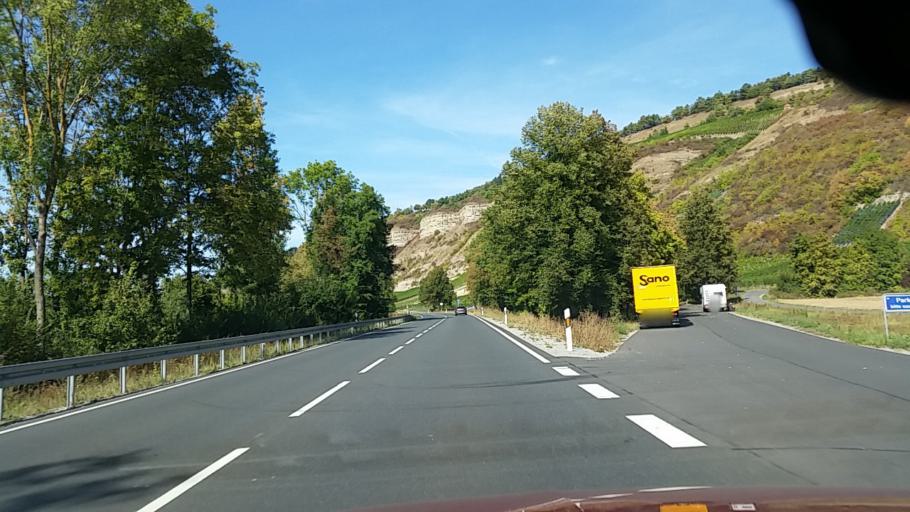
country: DE
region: Bavaria
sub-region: Regierungsbezirk Unterfranken
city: Zellingen
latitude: 49.8916
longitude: 9.8353
